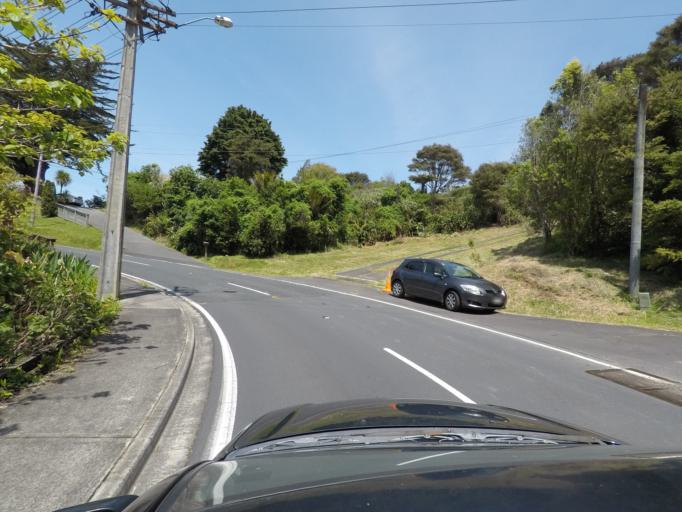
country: NZ
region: Auckland
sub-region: Auckland
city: Titirangi
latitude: -36.9654
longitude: 174.6383
